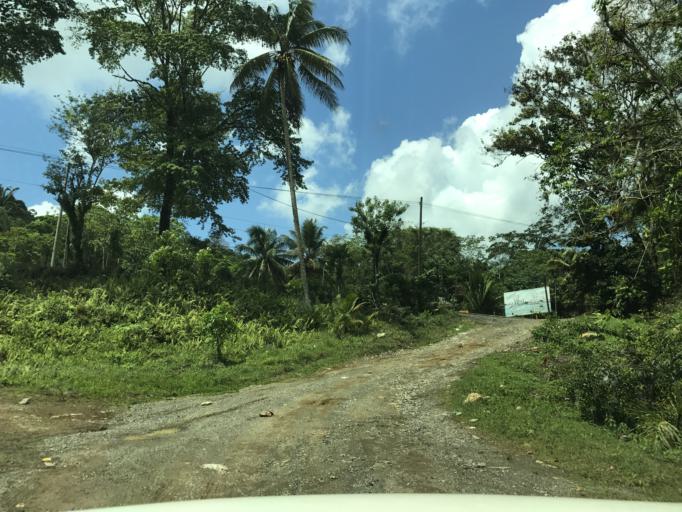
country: GT
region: Izabal
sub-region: Municipio de Puerto Barrios
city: Puerto Barrios
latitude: 15.6640
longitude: -88.5563
